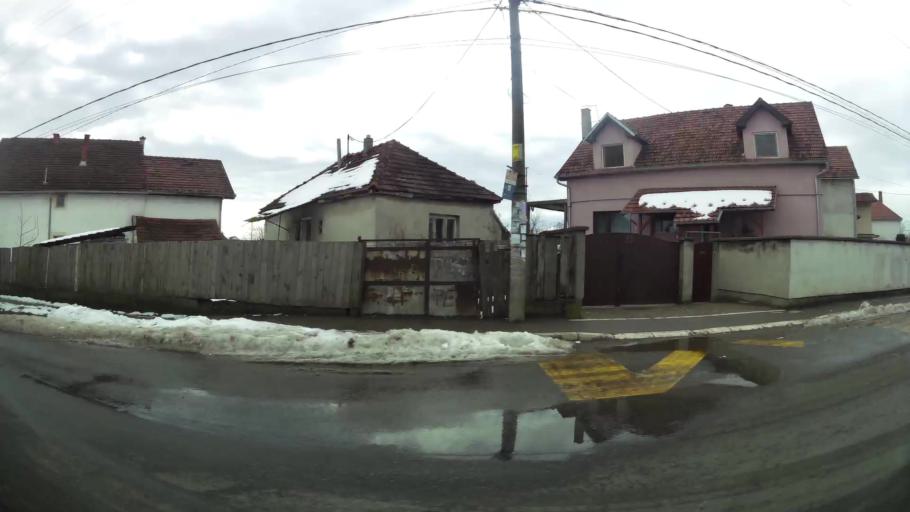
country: RS
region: Central Serbia
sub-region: Belgrade
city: Surcin
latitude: 44.7976
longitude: 20.2656
